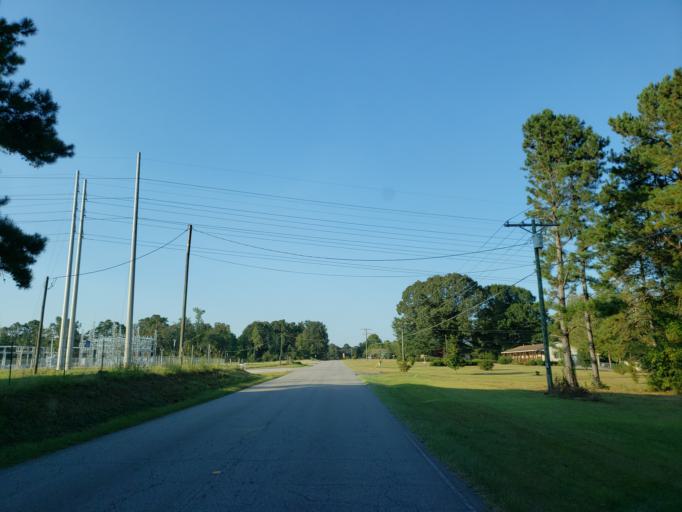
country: US
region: Mississippi
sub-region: Lamar County
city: West Hattiesburg
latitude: 31.3298
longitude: -89.4470
